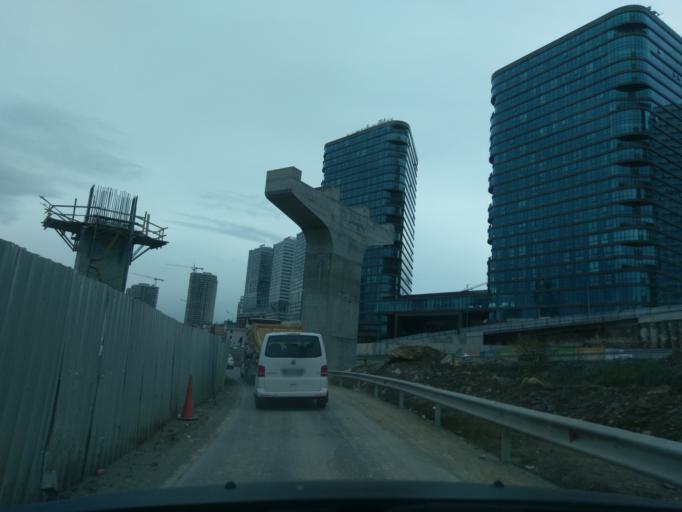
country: TR
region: Istanbul
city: UEskuedar
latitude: 40.9975
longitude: 29.0557
